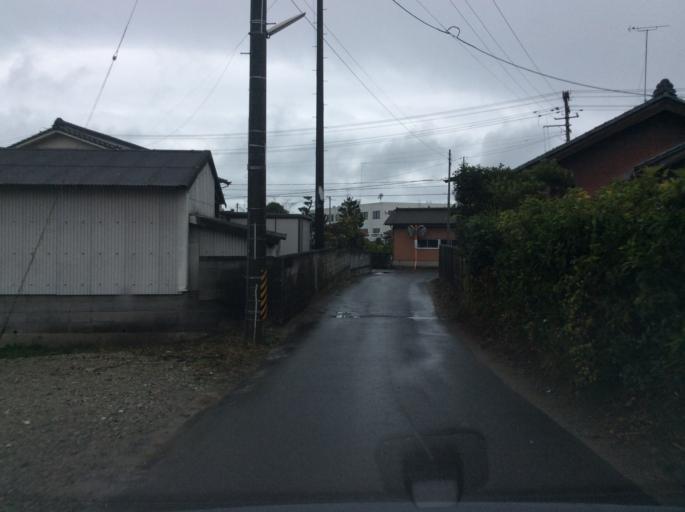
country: JP
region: Fukushima
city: Iwaki
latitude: 37.0871
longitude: 140.9652
